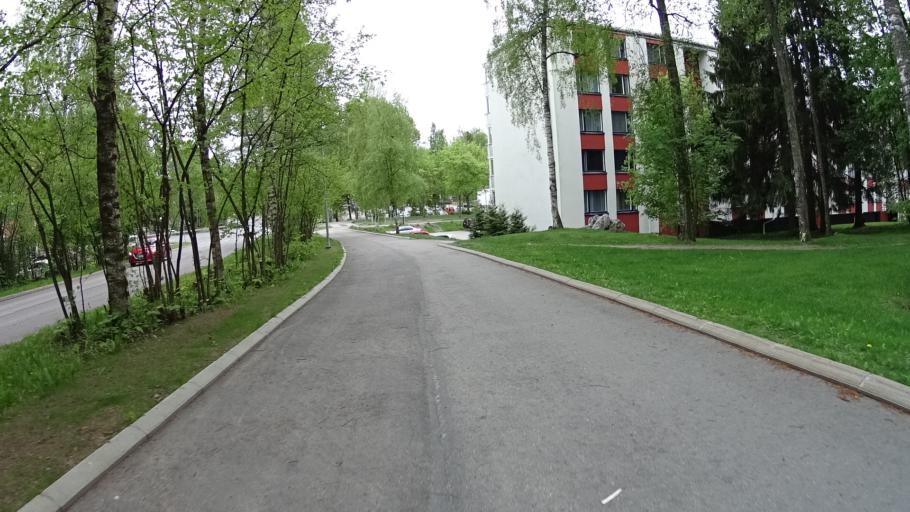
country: FI
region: Uusimaa
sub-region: Helsinki
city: Kilo
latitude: 60.2635
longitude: 24.8052
